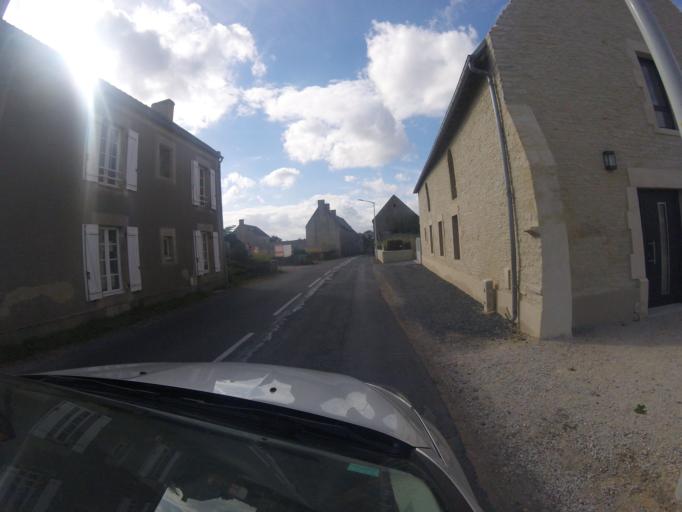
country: FR
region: Lower Normandy
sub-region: Departement du Calvados
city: Saint-Vigor-le-Grand
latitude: 49.3355
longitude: -0.6945
